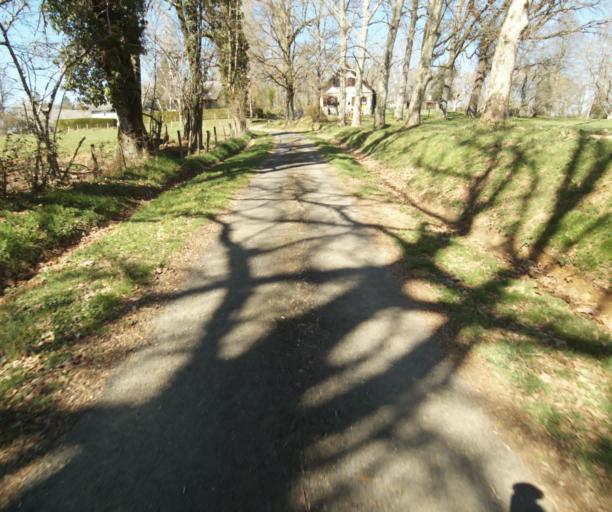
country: FR
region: Limousin
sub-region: Departement de la Correze
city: Saint-Clement
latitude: 45.3920
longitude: 1.6613
